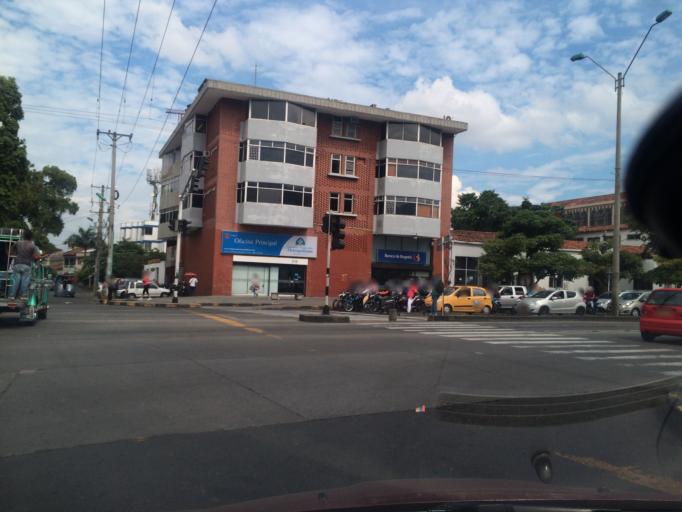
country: CO
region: Valle del Cauca
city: Cali
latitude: 3.4341
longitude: -76.5418
